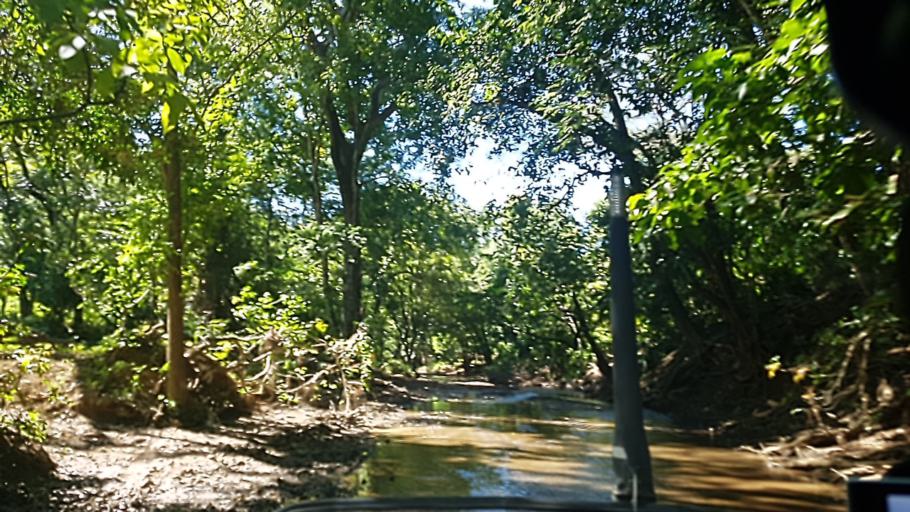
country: NI
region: Rivas
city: Tola
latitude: 11.5477
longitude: -86.0931
